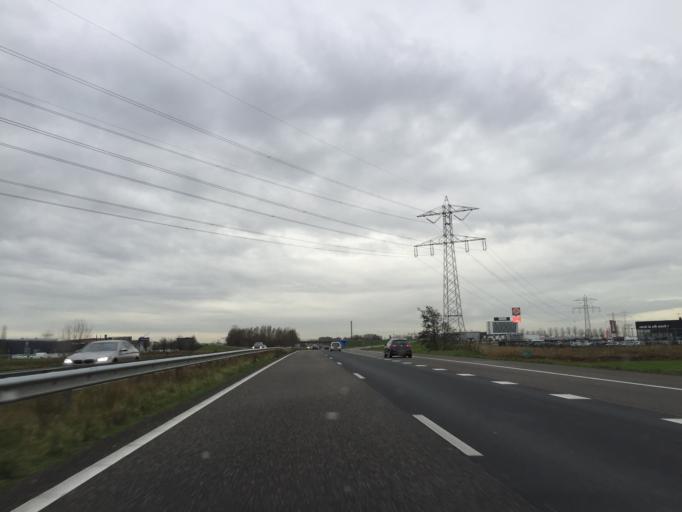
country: NL
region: North Brabant
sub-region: Roosendaal
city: Roosendaal
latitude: 51.5619
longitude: 4.4629
